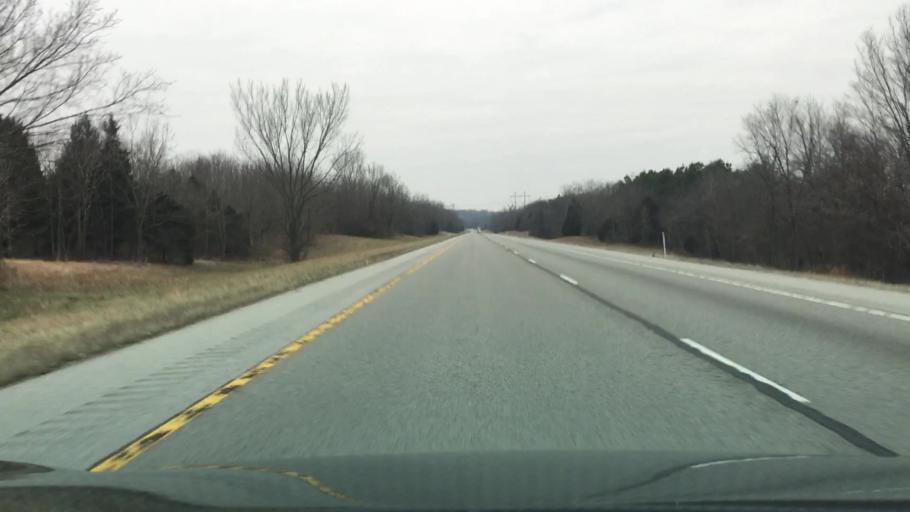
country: US
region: Illinois
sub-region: Johnson County
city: Vienna
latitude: 37.3600
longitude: -88.7950
